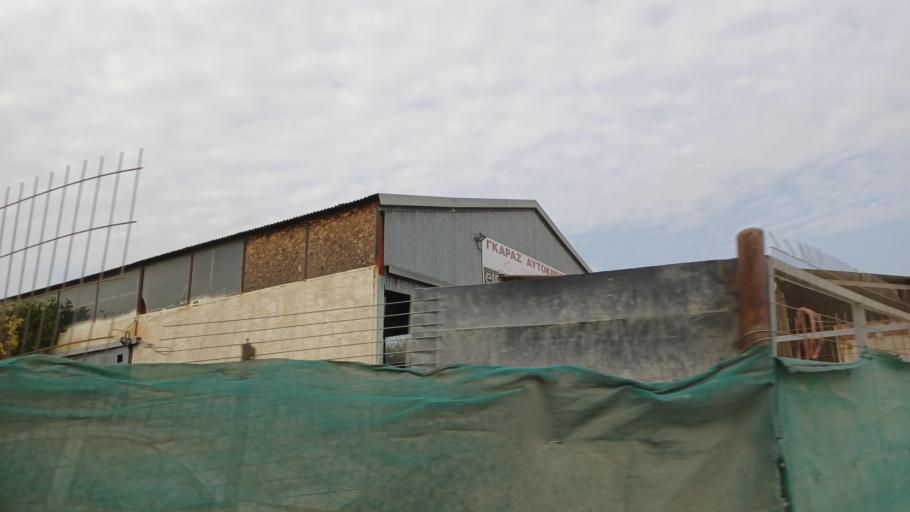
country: CY
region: Limassol
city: Ypsonas
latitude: 34.6749
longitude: 32.9517
